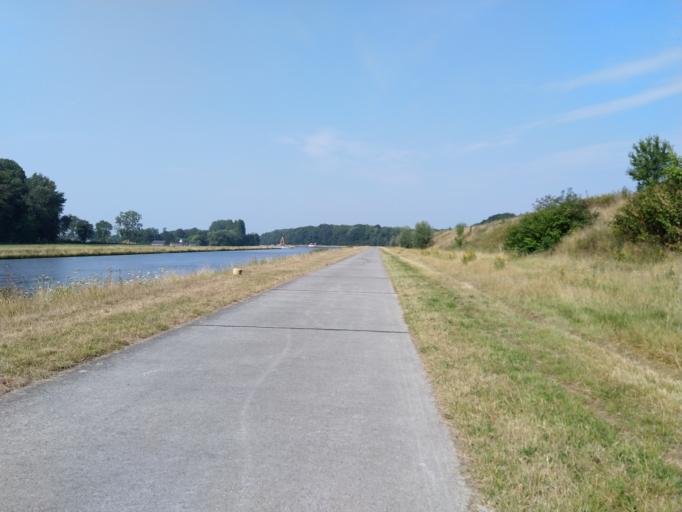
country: BE
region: Wallonia
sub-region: Province du Hainaut
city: La Louviere
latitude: 50.5006
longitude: 4.1669
